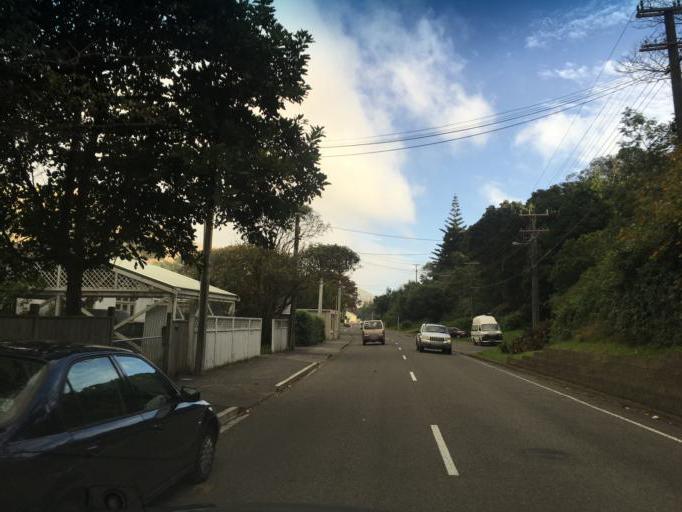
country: NZ
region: Wellington
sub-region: Kapiti Coast District
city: Paraparaumu
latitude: -40.9859
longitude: 174.9532
